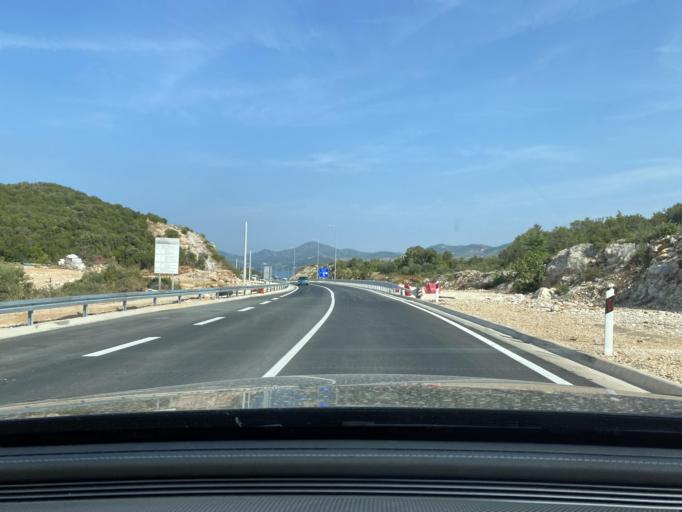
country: BA
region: Federation of Bosnia and Herzegovina
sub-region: Hercegovacko-Bosanski Kanton
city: Neum
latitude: 42.9167
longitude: 17.5281
